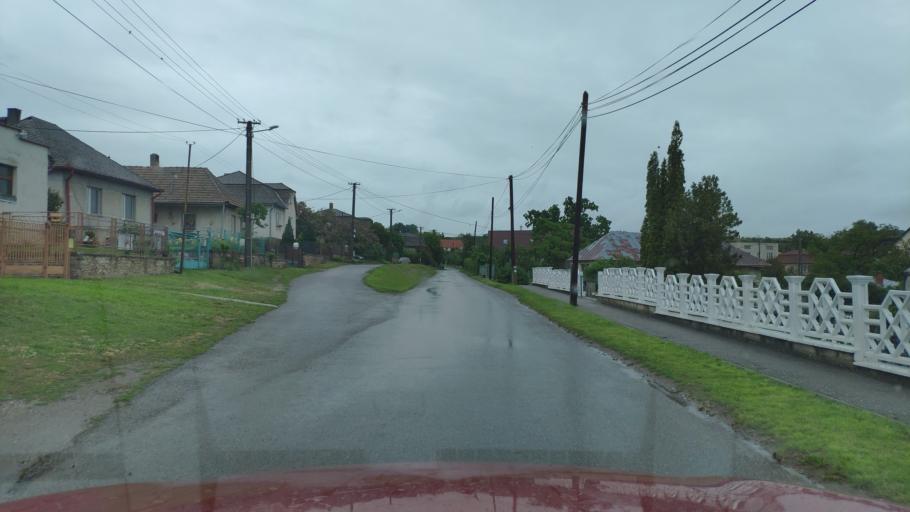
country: HU
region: Borsod-Abauj-Zemplen
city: Satoraljaujhely
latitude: 48.4242
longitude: 21.7156
